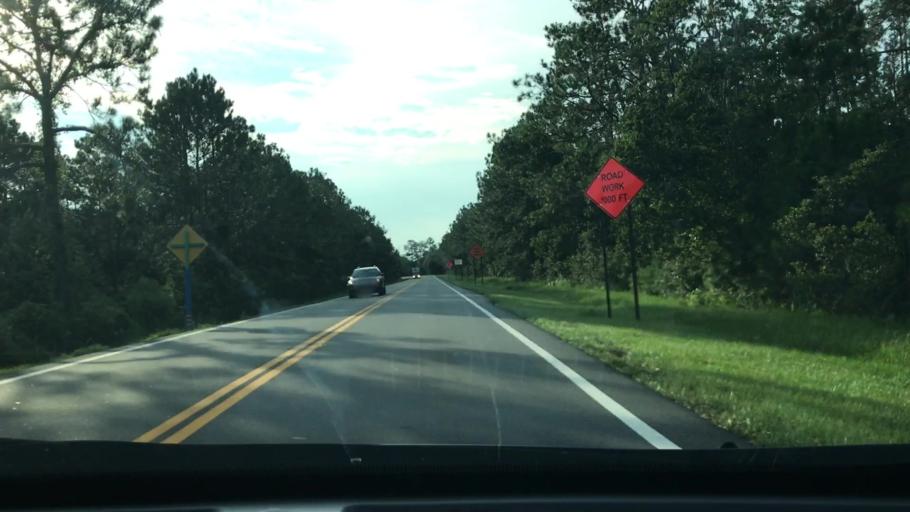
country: US
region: Florida
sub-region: Osceola County
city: Celebration
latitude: 28.3920
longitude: -81.5647
